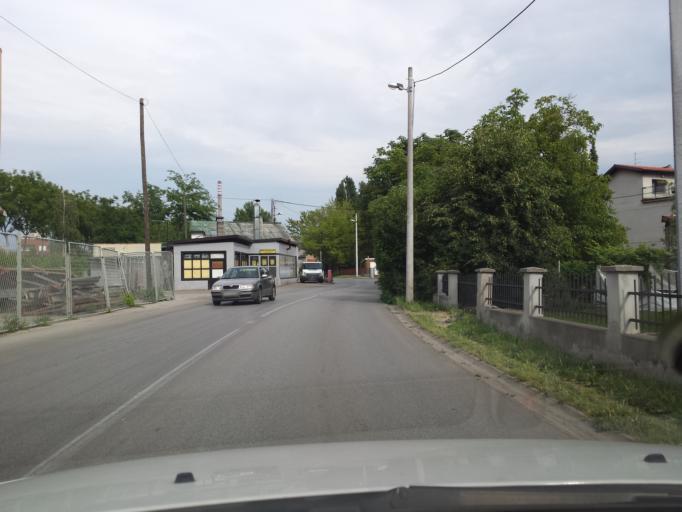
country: HR
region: Grad Zagreb
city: Jankomir
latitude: 45.8086
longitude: 15.9332
